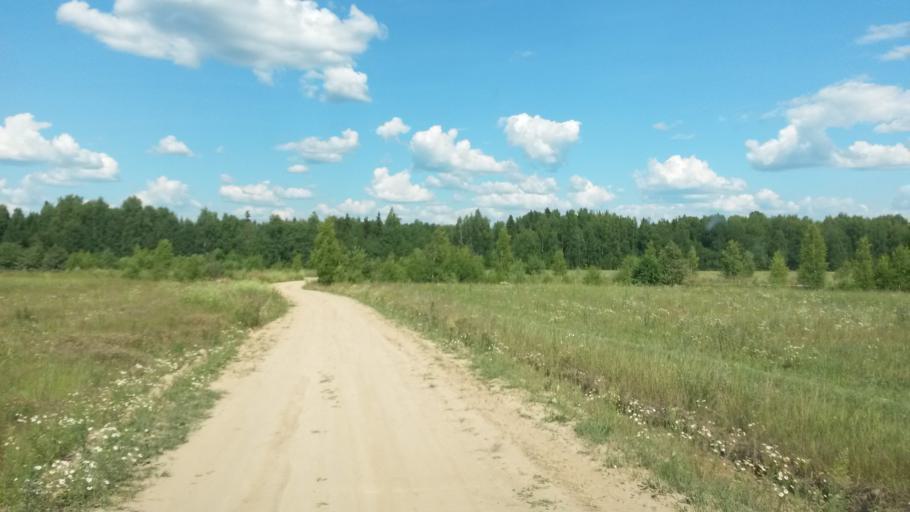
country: RU
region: Ivanovo
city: Zarechnyy
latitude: 57.4819
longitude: 42.3449
